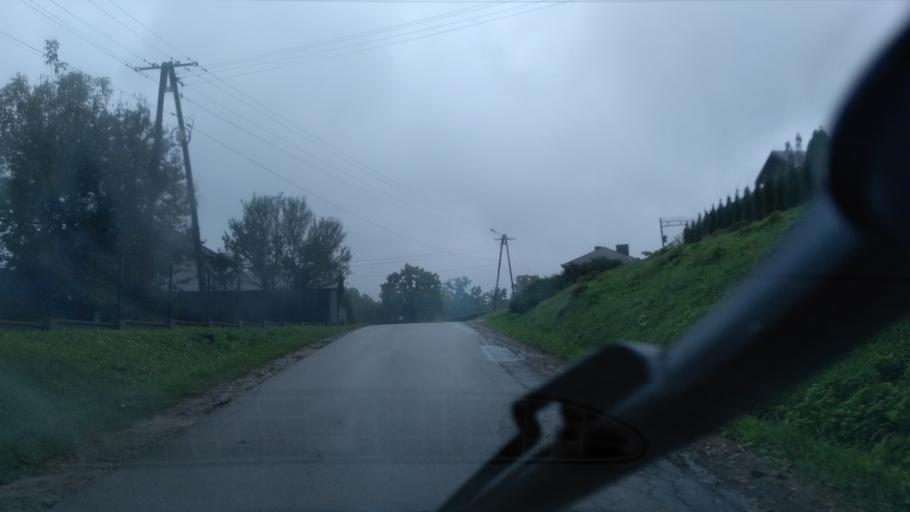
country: PL
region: Subcarpathian Voivodeship
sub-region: Powiat ropczycko-sedziszowski
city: Niedzwiada
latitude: 50.0246
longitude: 21.5407
